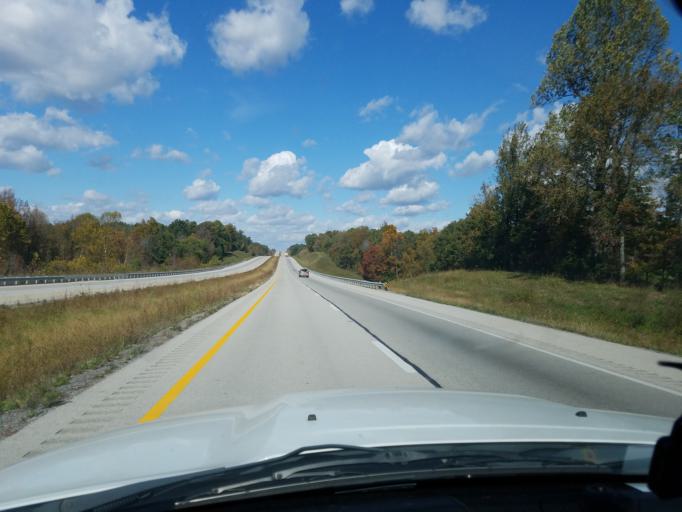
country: US
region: Kentucky
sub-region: Ohio County
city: Hartford
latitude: 37.5053
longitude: -86.9143
